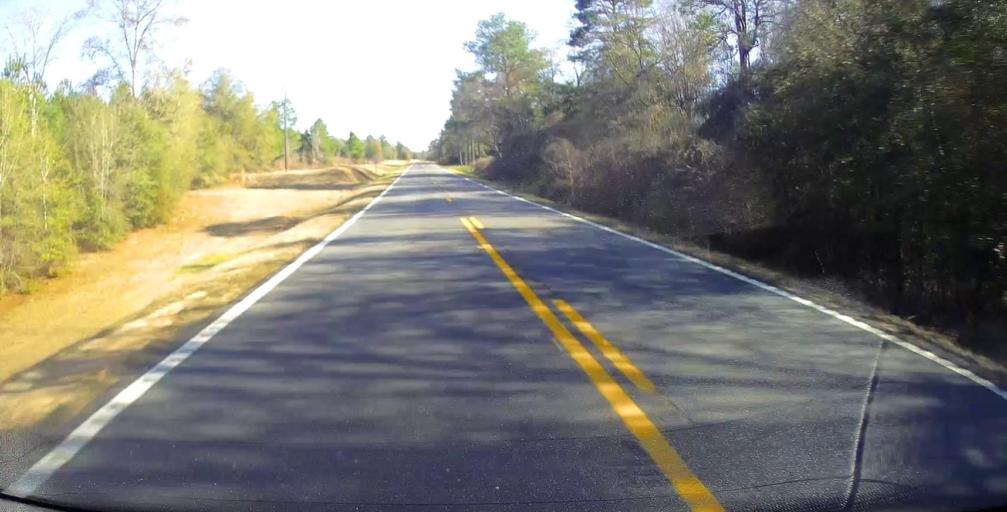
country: US
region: Georgia
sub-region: Taylor County
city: Butler
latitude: 32.4306
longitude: -84.2471
